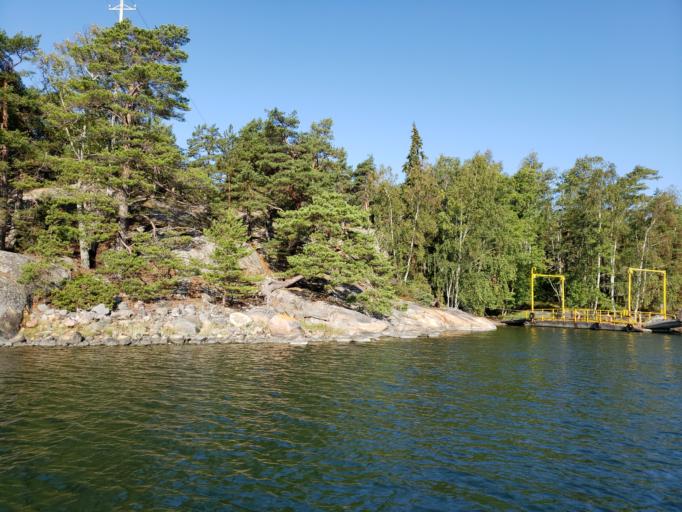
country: FI
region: Varsinais-Suomi
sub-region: Aboland-Turunmaa
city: Dragsfjaerd
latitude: 59.9138
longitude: 22.3790
